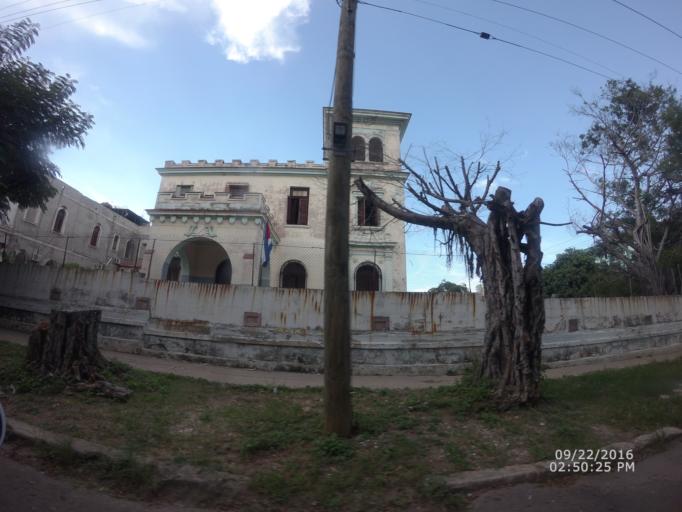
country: CU
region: La Habana
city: Havana
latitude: 23.1372
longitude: -82.3908
